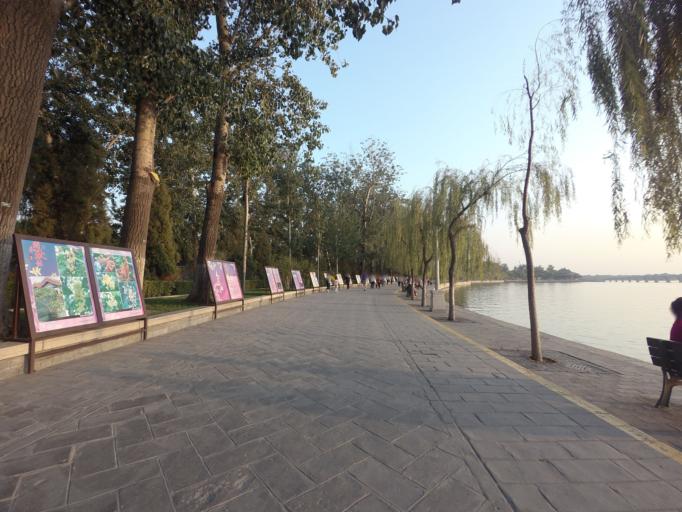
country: CN
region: Beijing
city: Haidian
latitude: 39.9933
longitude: 116.2744
